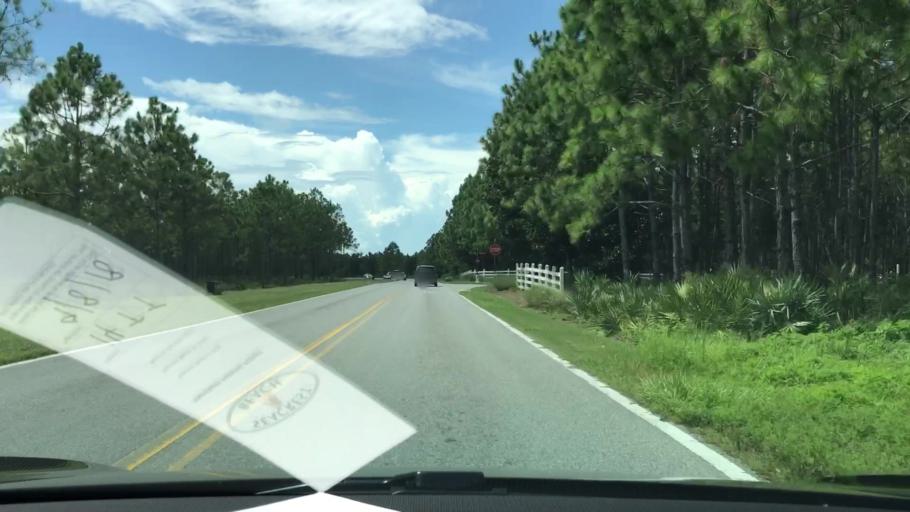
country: US
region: Florida
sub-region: Walton County
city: Seaside
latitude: 30.2937
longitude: -86.0325
